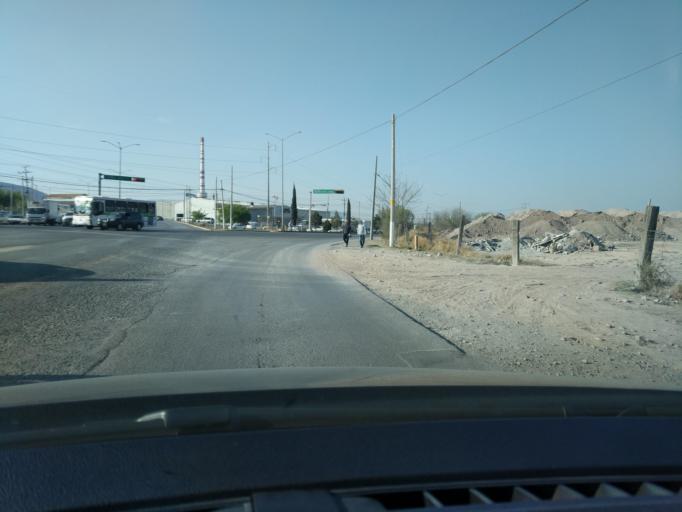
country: MX
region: Coahuila
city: Saltillo
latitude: 25.4783
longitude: -100.9839
